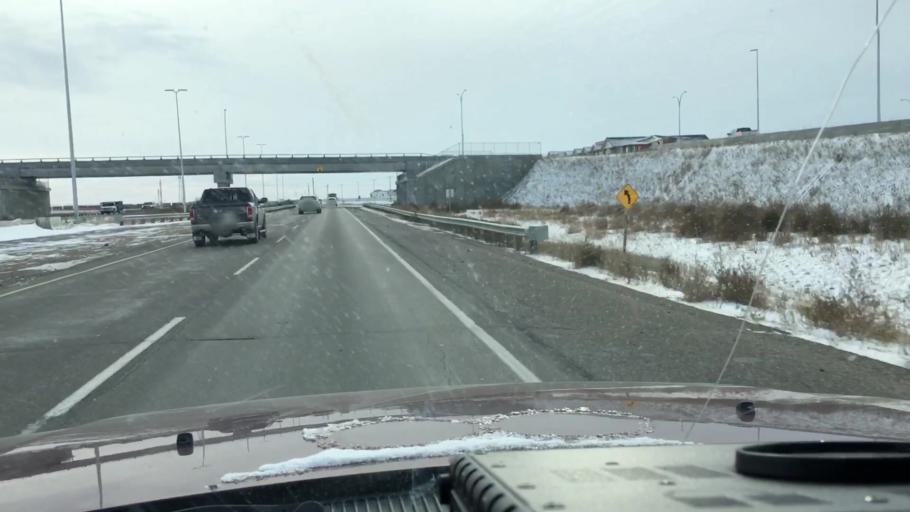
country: CA
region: Saskatchewan
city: Saskatoon
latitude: 52.0795
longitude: -106.6050
